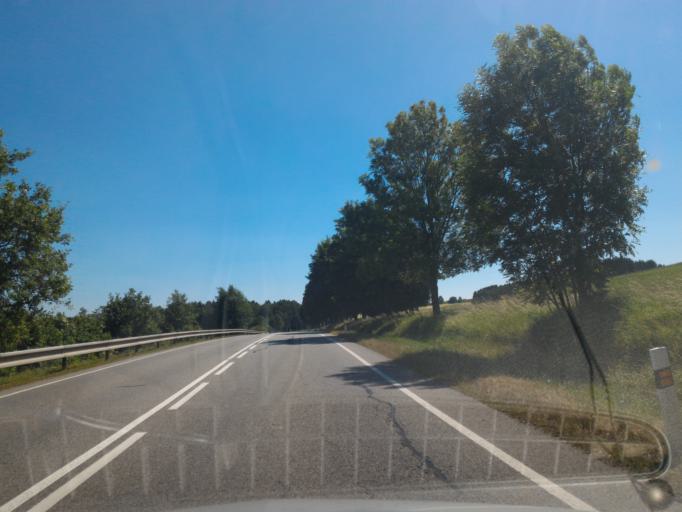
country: CZ
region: Vysocina
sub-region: Okres Jihlava
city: Trest'
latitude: 49.3130
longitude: 15.4805
